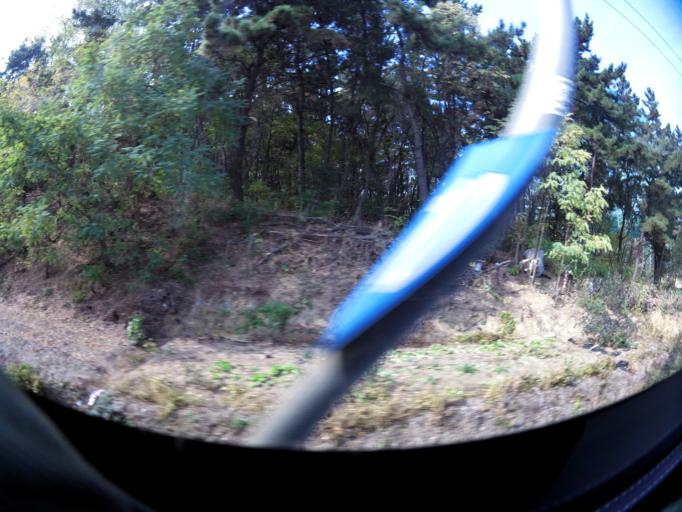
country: KR
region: Gyeongsangbuk-do
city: Gumi
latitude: 36.1045
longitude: 128.3591
